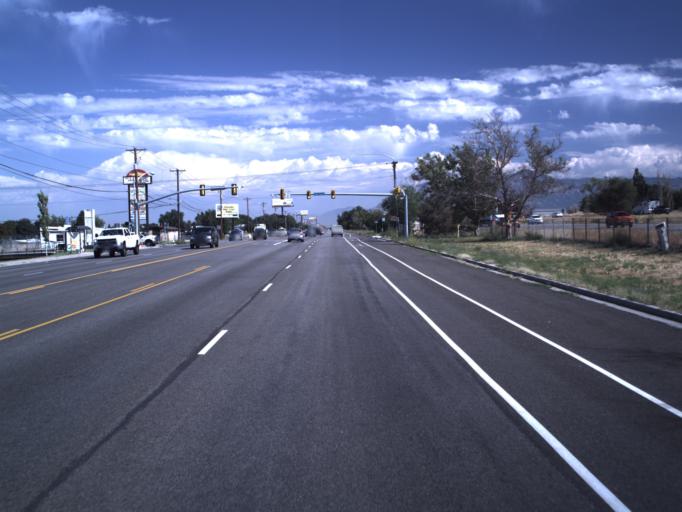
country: US
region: Utah
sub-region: Davis County
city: Sunset
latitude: 41.1315
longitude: -112.0260
